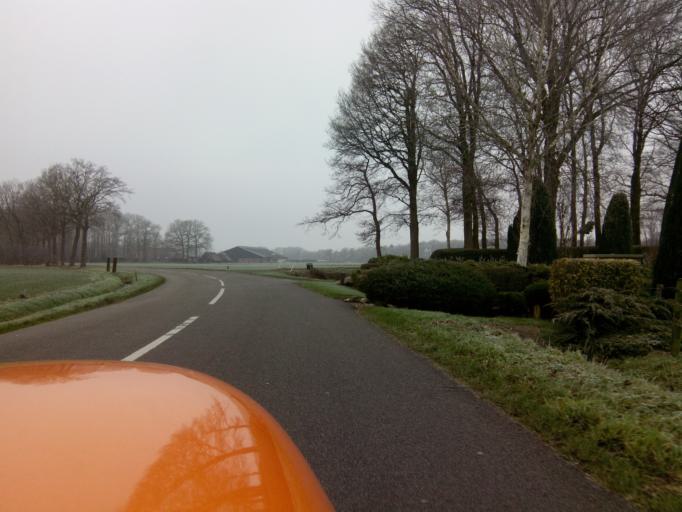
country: NL
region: Gelderland
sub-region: Gemeente Barneveld
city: Voorthuizen
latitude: 52.1930
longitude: 5.5997
